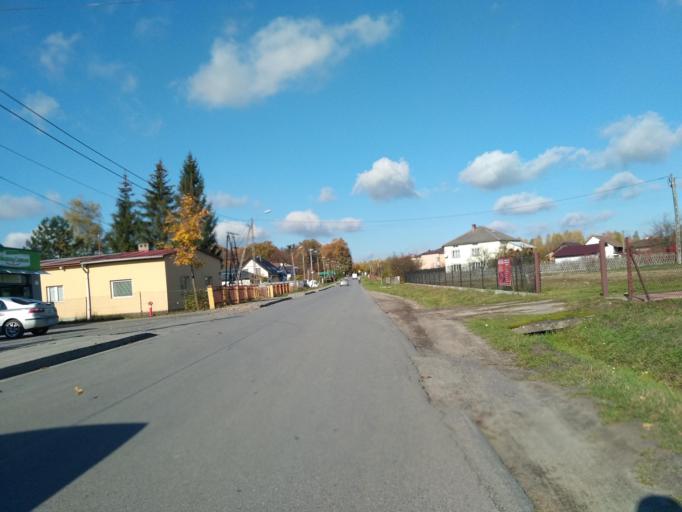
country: PL
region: Subcarpathian Voivodeship
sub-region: Powiat rzeszowski
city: Glogow Malopolski
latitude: 50.1565
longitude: 21.9094
